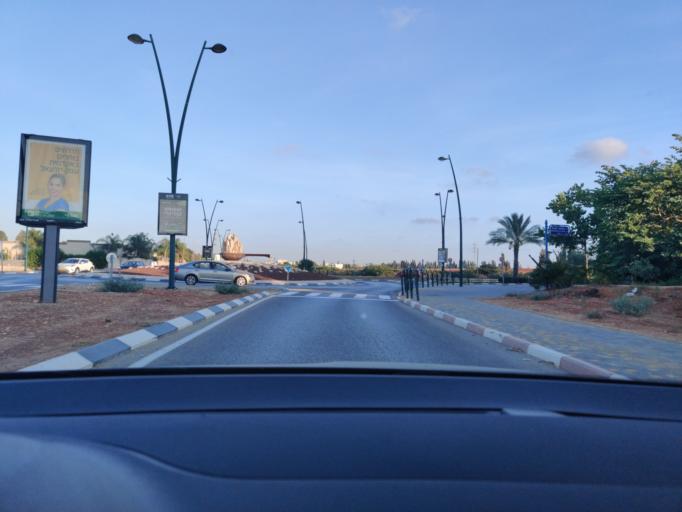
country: IL
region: Central District
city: Elyakhin
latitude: 32.4276
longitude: 34.9412
